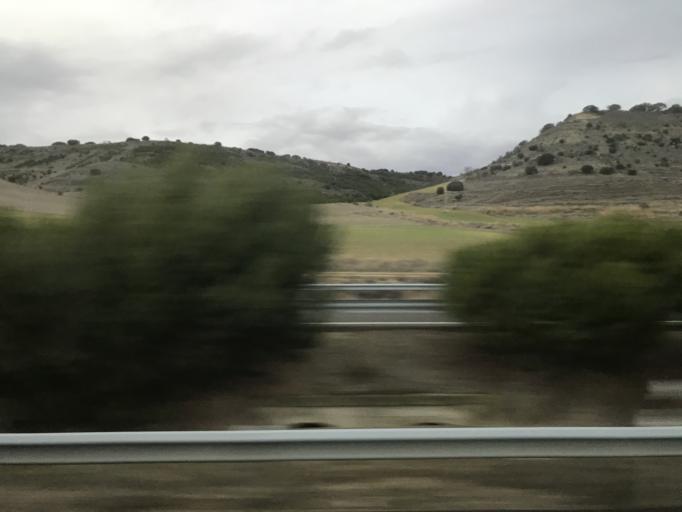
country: ES
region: Castille and Leon
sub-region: Provincia de Palencia
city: Palenzuela
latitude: 42.1109
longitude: -4.1679
